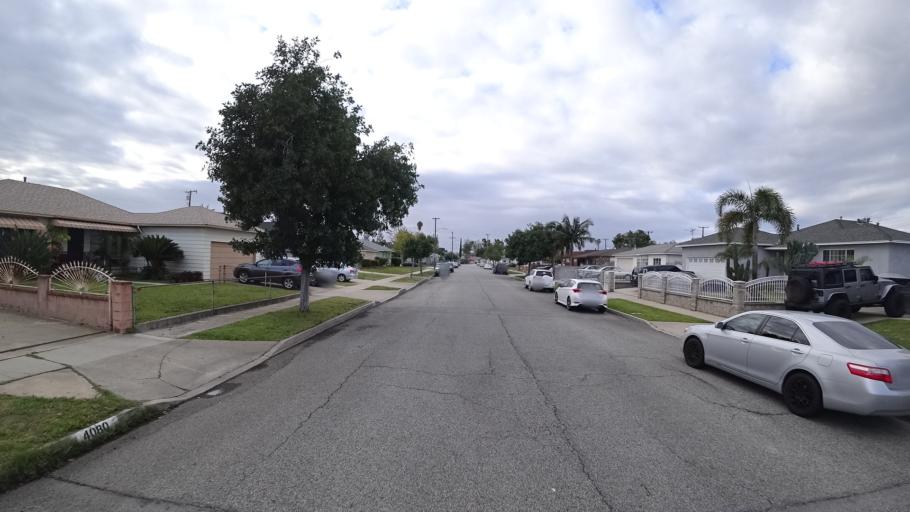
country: US
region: California
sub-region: Los Angeles County
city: Baldwin Park
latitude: 34.0865
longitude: -117.9713
